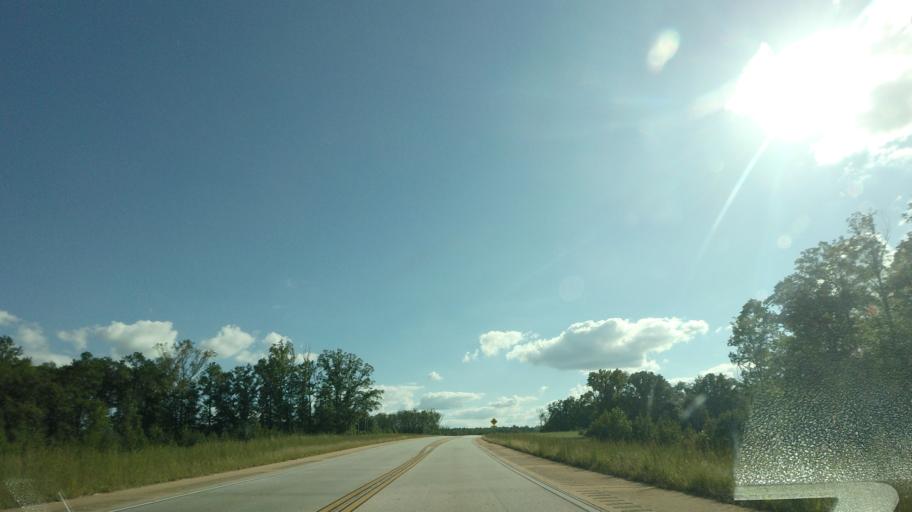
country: US
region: Georgia
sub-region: Lamar County
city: Barnesville
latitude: 33.0432
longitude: -84.1324
